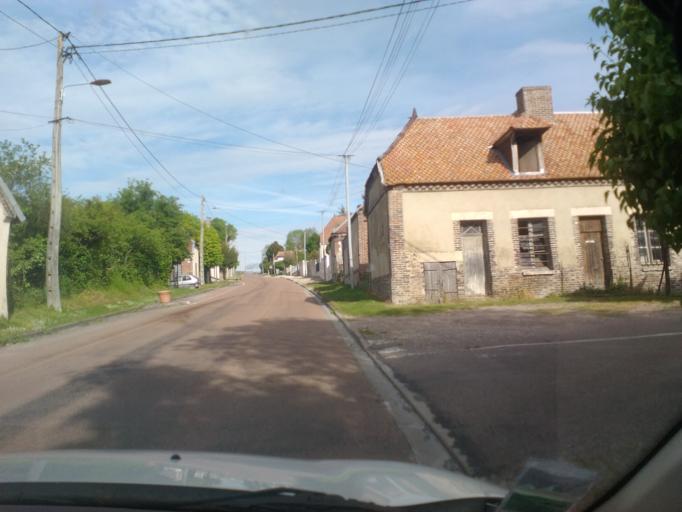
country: FR
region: Champagne-Ardenne
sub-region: Departement de l'Aube
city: Payns
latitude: 48.3709
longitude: 3.8960
